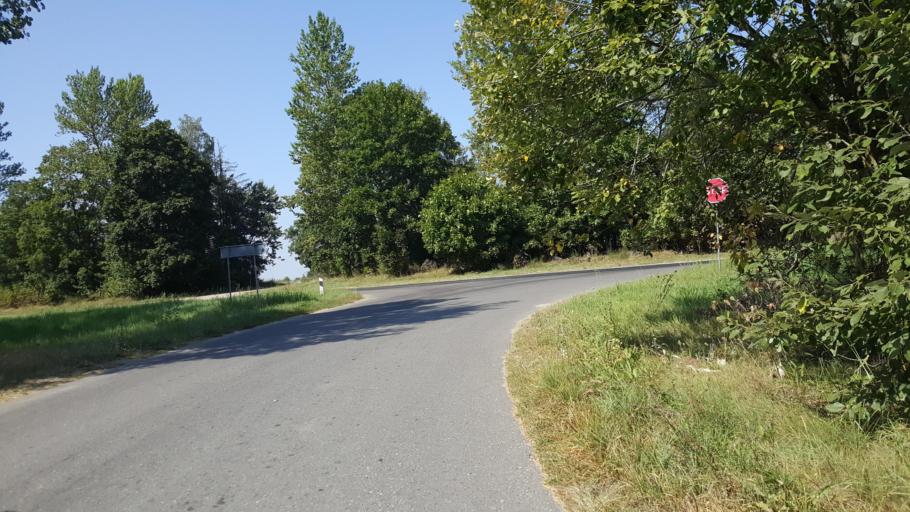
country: BY
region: Brest
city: Vysokaye
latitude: 52.4287
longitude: 23.4401
